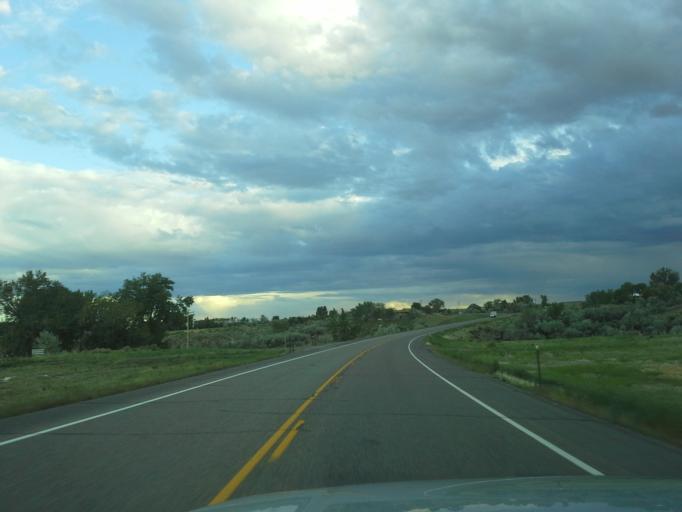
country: US
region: Wyoming
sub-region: Big Horn County
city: Basin
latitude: 44.3583
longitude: -108.0394
